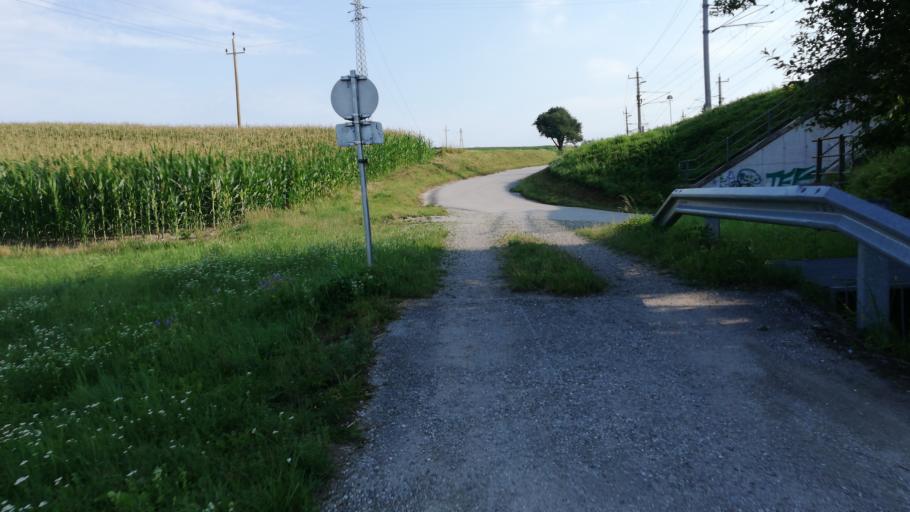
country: AT
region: Upper Austria
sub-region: Wels-Land
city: Buchkirchen
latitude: 48.1997
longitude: 13.9745
